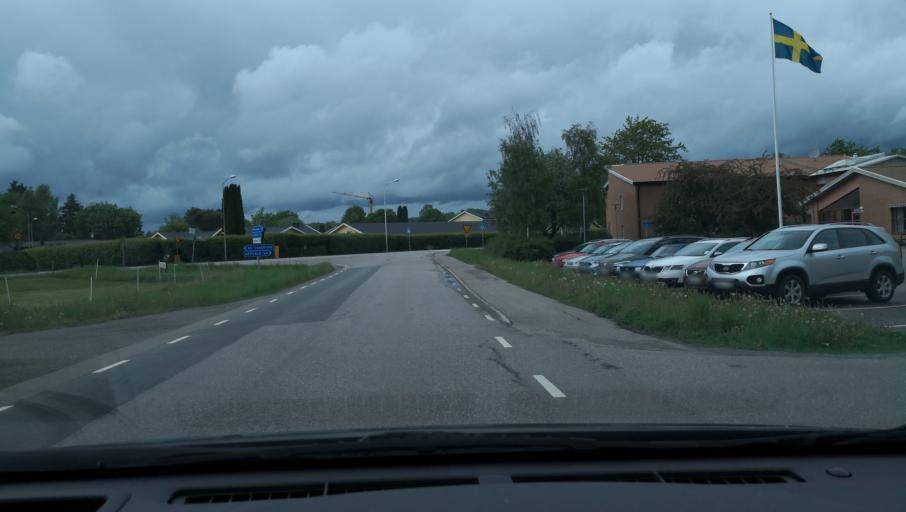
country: SE
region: Uppsala
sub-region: Enkopings Kommun
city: Orsundsbro
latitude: 59.7306
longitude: 17.3060
